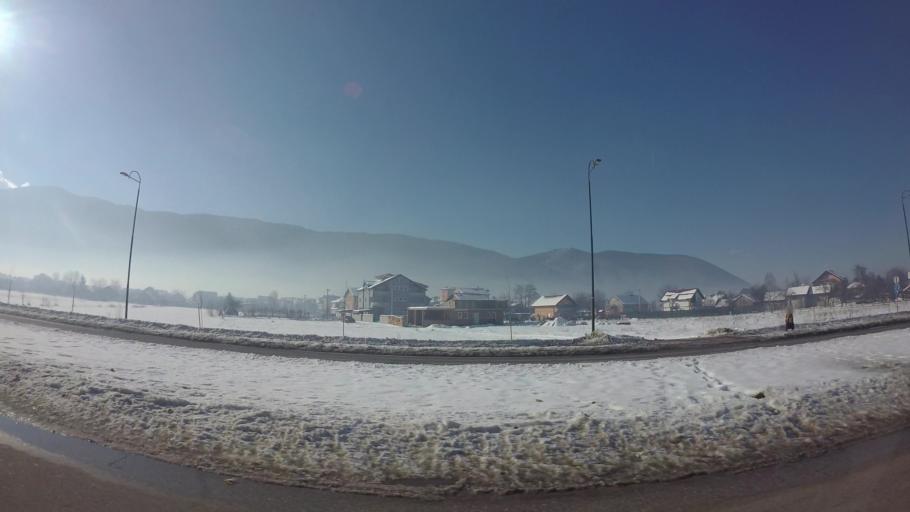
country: BA
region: Federation of Bosnia and Herzegovina
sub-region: Kanton Sarajevo
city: Sarajevo
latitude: 43.8140
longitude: 18.3093
